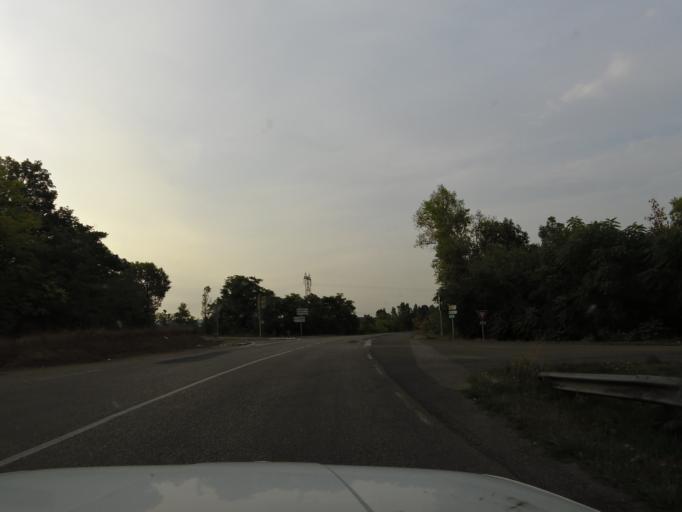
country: FR
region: Rhone-Alpes
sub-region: Departement de l'Ain
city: Saint-Jean-de-Niost
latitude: 45.8144
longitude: 5.2144
